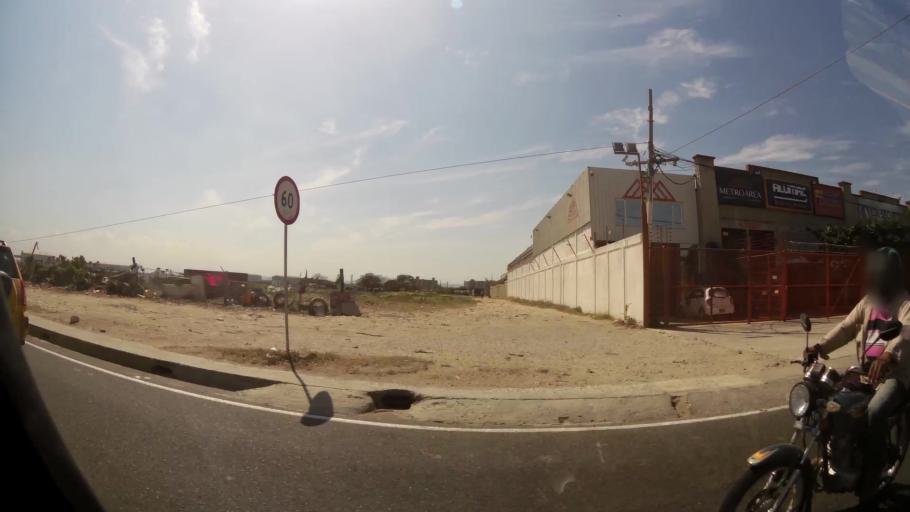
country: CO
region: Atlantico
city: Barranquilla
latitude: 10.9601
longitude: -74.8375
